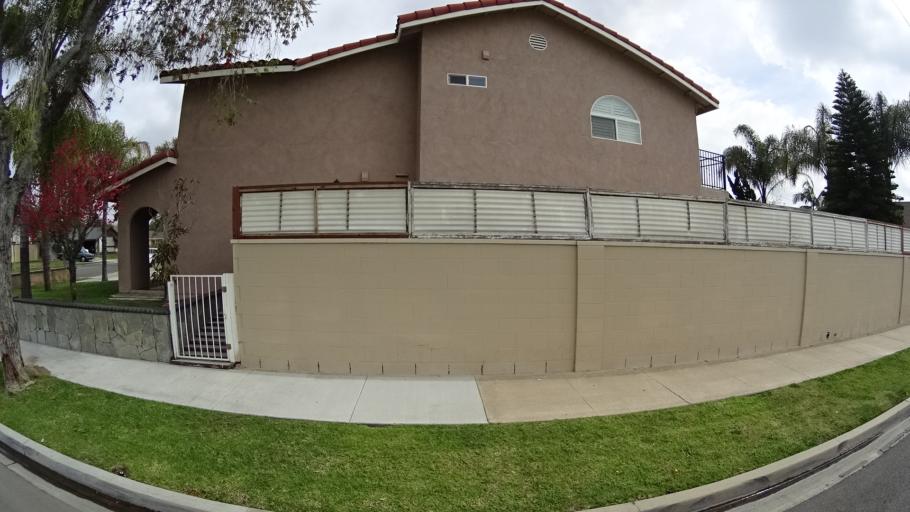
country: US
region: California
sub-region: Orange County
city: Stanton
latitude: 33.8270
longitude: -117.9918
